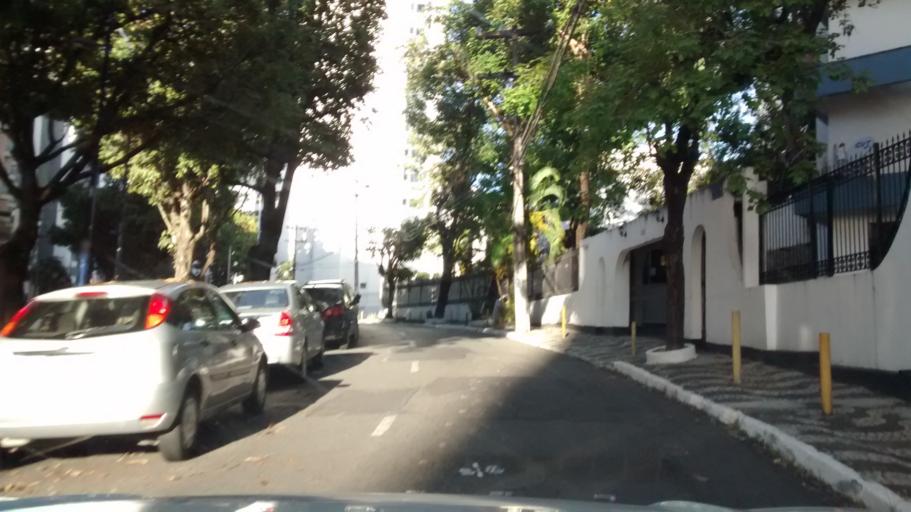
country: BR
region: Bahia
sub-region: Salvador
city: Salvador
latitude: -13.0052
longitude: -38.5202
